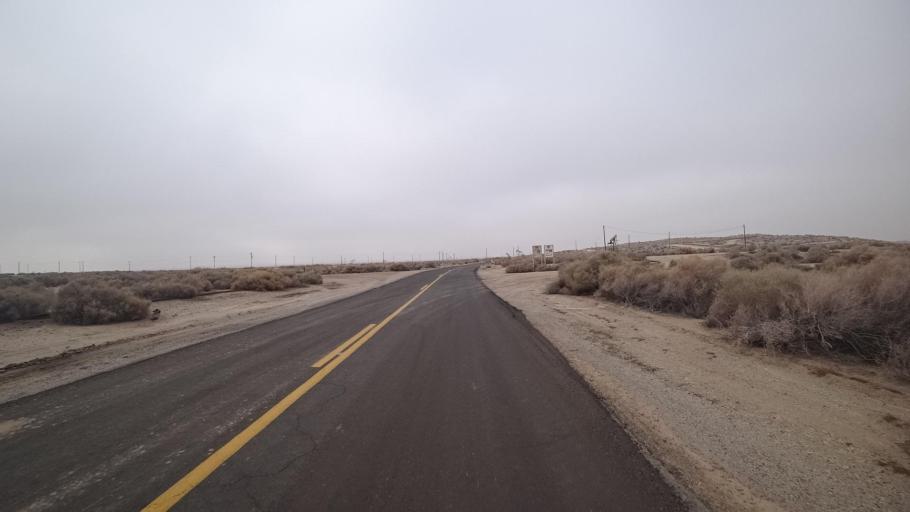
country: US
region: California
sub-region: Kern County
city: Maricopa
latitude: 35.0754
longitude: -119.3564
